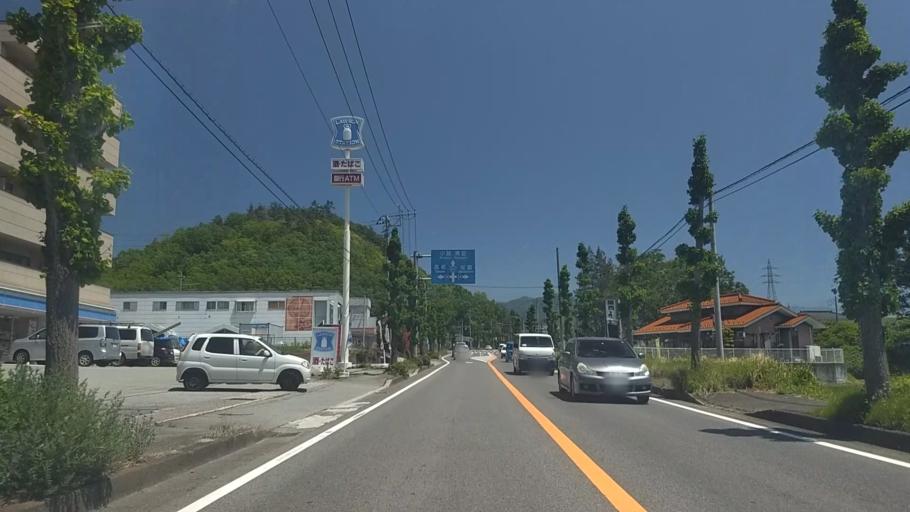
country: JP
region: Yamanashi
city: Nirasaki
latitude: 35.7927
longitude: 138.4202
